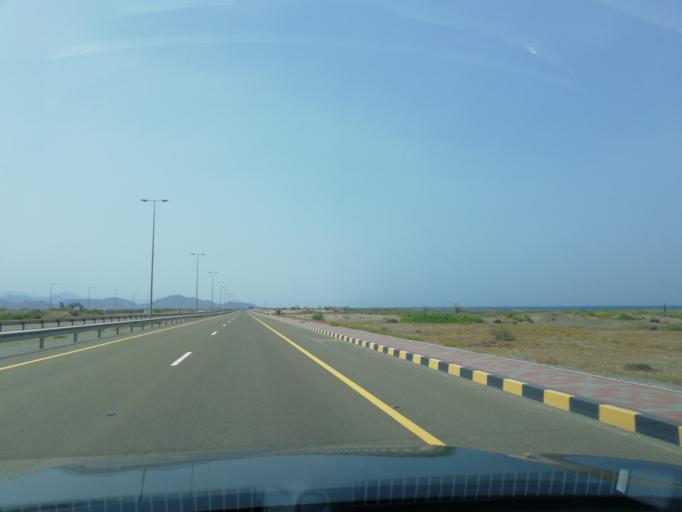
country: OM
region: Al Batinah
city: Shinas
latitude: 24.9082
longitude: 56.3931
